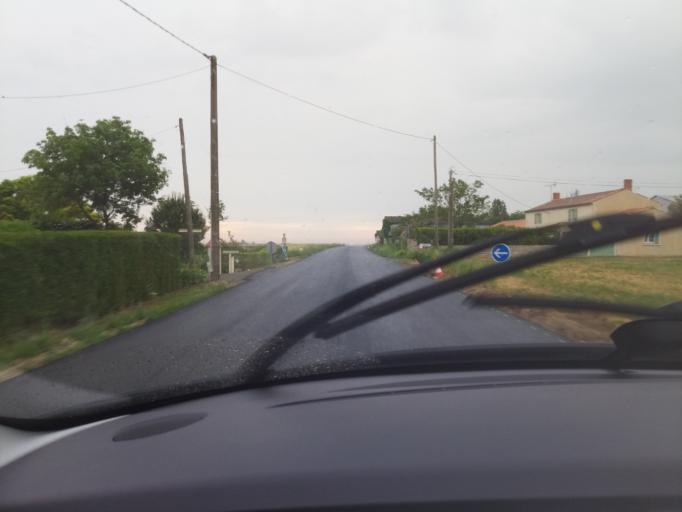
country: FR
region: Poitou-Charentes
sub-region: Departement de la Charente-Maritime
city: Marans
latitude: 46.2897
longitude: -0.9523
